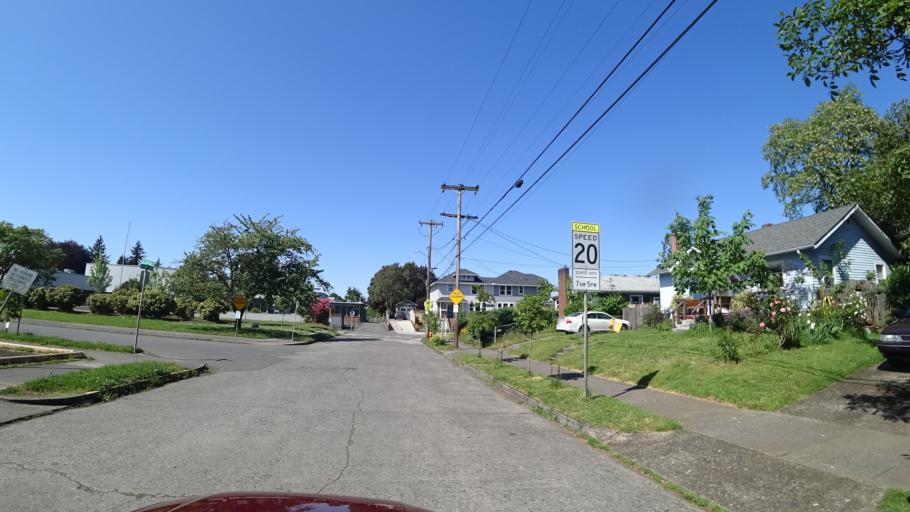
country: US
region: Oregon
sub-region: Multnomah County
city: Lents
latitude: 45.4947
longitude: -122.6132
